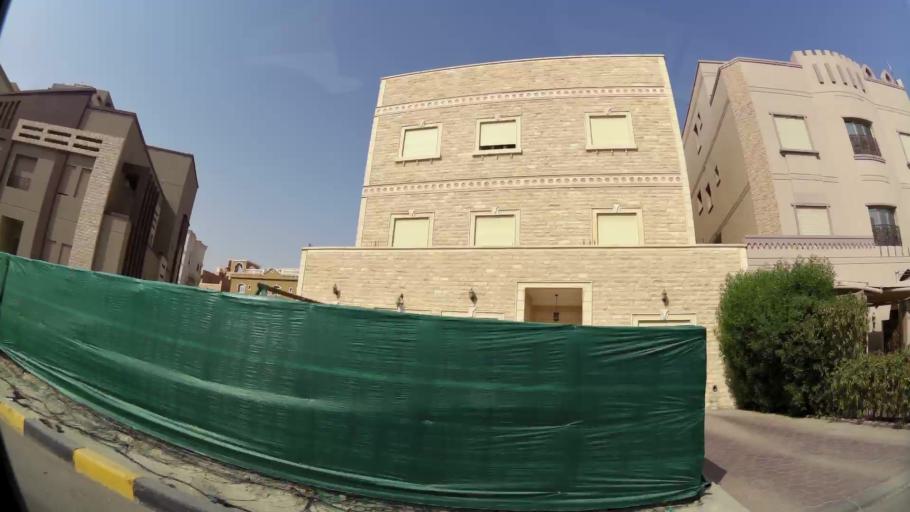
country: KW
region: Muhafazat al Jahra'
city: Al Jahra'
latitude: 29.3339
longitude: 47.7604
